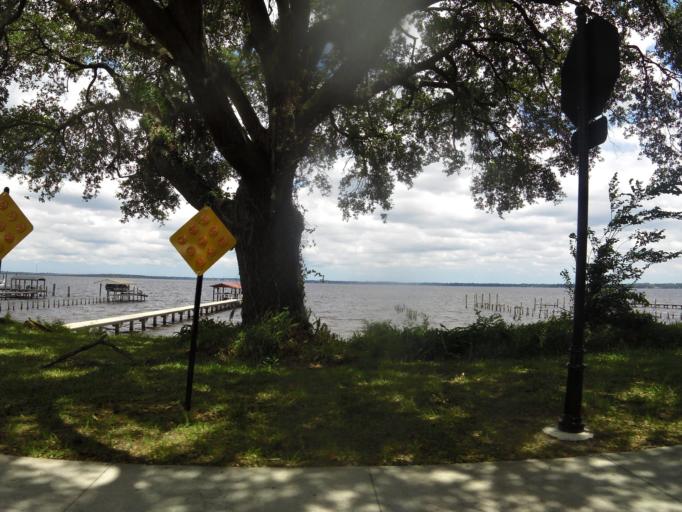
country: US
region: Florida
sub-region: Clay County
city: Orange Park
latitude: 30.1779
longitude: -81.6983
